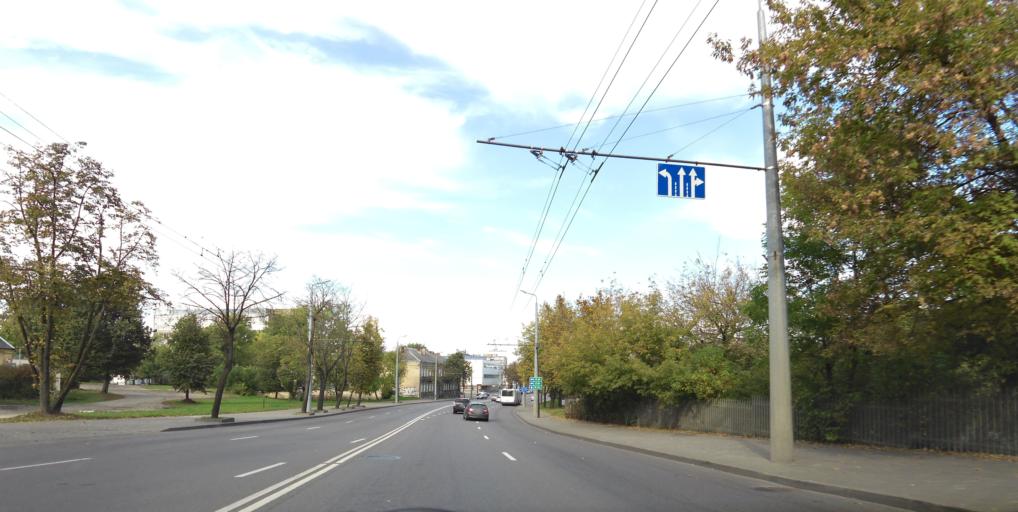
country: LT
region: Vilnius County
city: Naujamiestis
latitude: 54.6679
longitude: 25.2716
